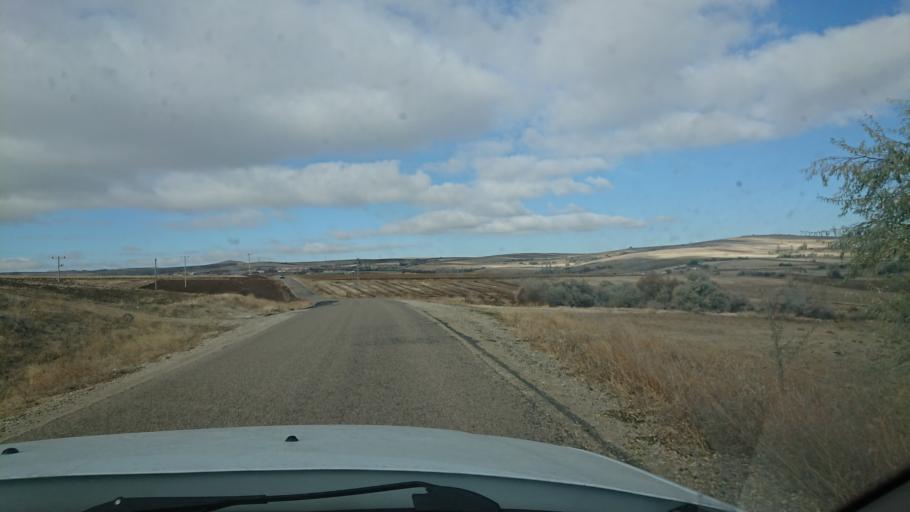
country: TR
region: Aksaray
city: Agacoren
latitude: 38.8191
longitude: 33.9769
